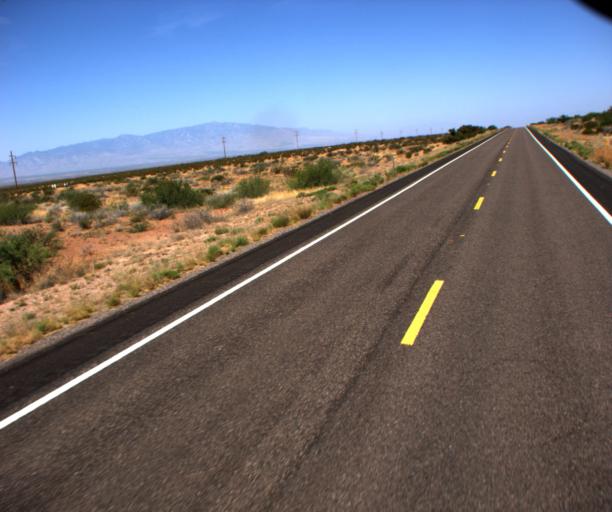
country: US
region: Arizona
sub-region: Graham County
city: Swift Trail Junction
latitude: 32.7558
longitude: -109.4238
